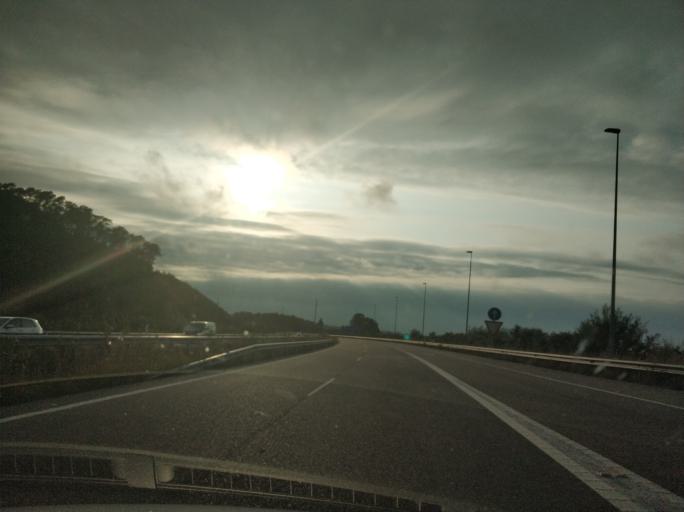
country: ES
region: Asturias
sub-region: Province of Asturias
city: Cudillero
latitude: 43.5574
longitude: -6.1740
